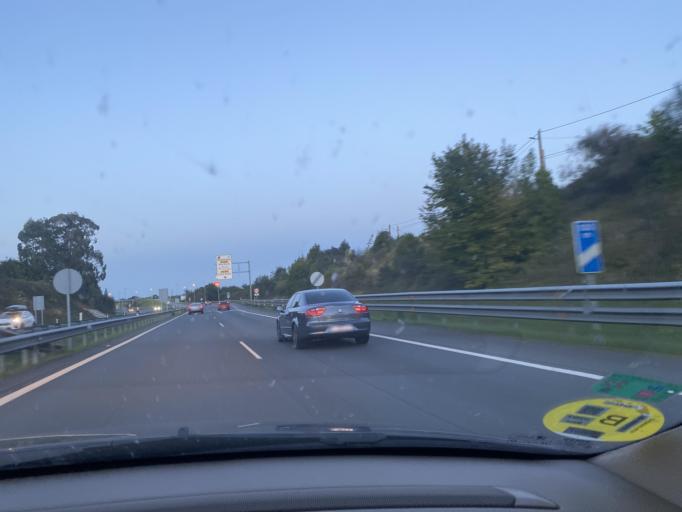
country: ES
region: Asturias
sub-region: Province of Asturias
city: Gijon
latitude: 43.4920
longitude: -5.6778
